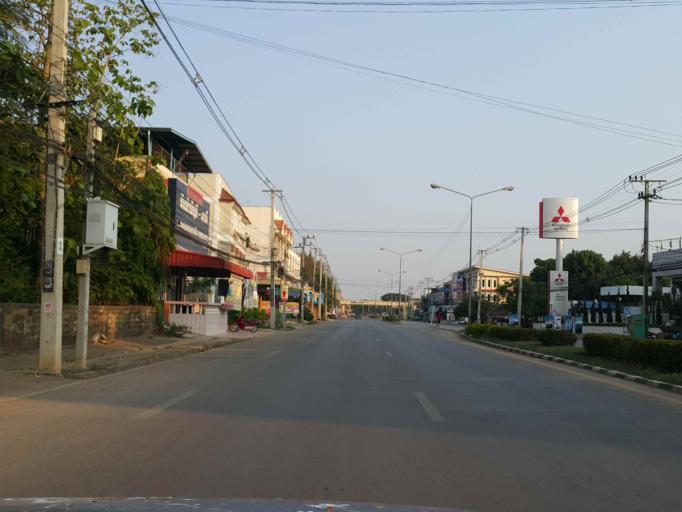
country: TH
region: Sukhothai
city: Sawankhalok
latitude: 17.2979
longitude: 99.8359
